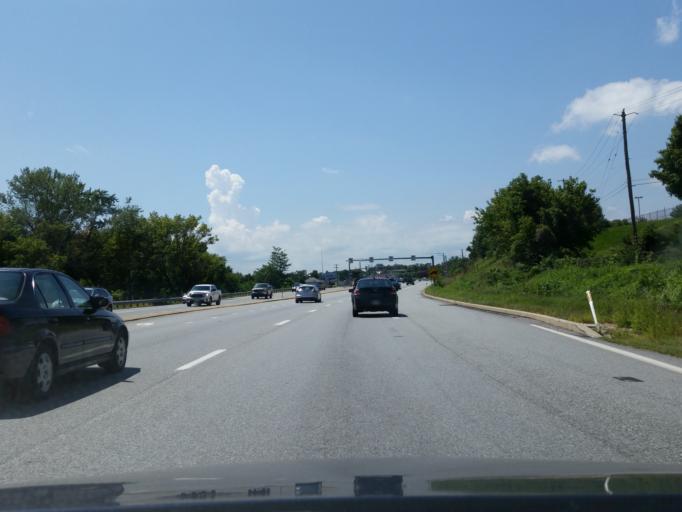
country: US
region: Pennsylvania
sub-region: York County
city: North York
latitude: 39.9825
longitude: -76.7121
